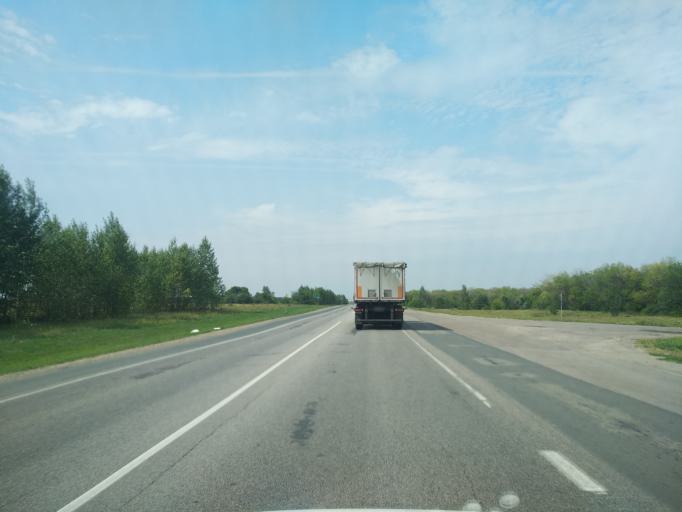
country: RU
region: Voronezj
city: Novaya Usman'
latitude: 51.7004
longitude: 39.4110
